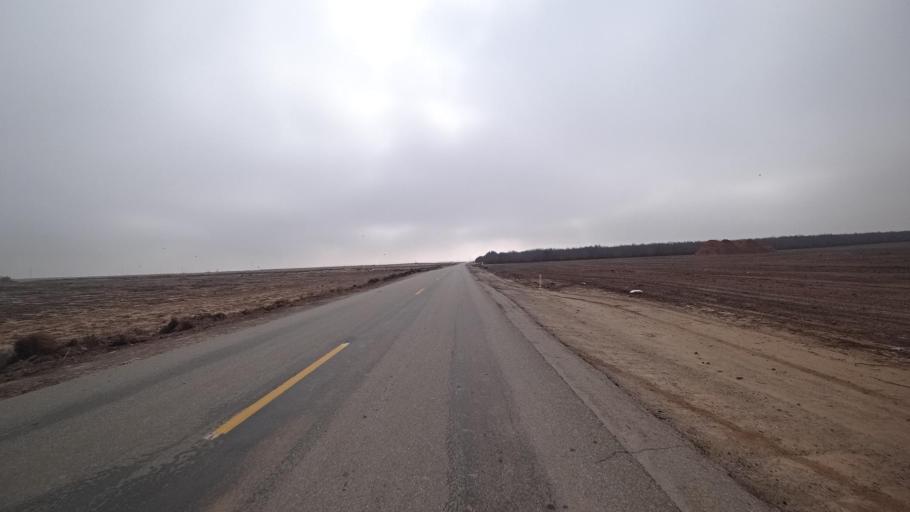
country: US
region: California
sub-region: Kern County
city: Maricopa
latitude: 35.0928
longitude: -119.3141
